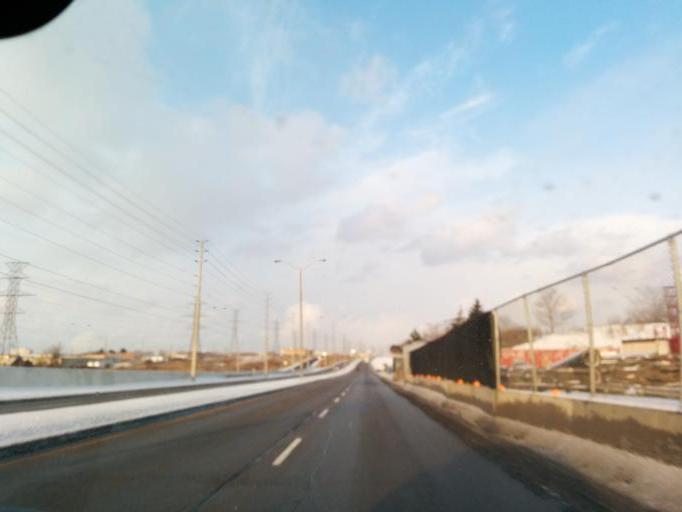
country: CA
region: Ontario
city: Mississauga
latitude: 43.6232
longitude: -79.6214
